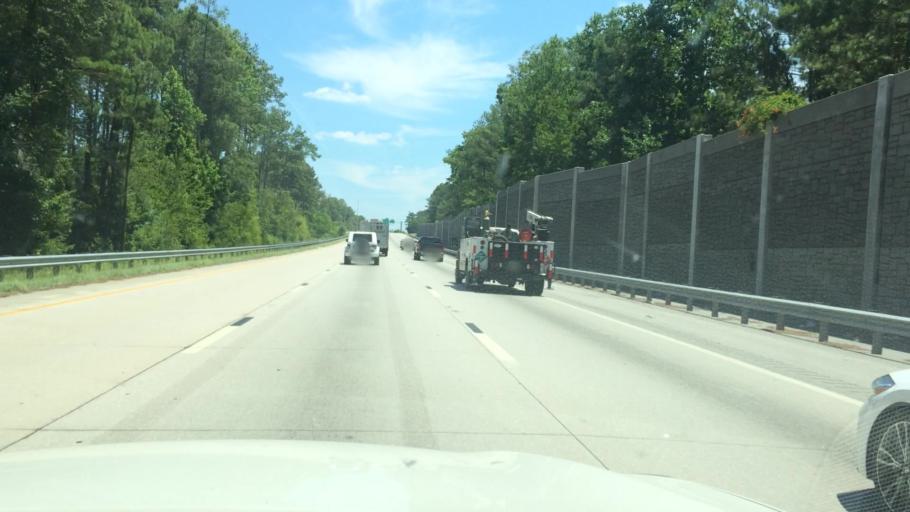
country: US
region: South Carolina
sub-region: Richland County
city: Woodfield
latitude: 34.0904
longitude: -80.8662
